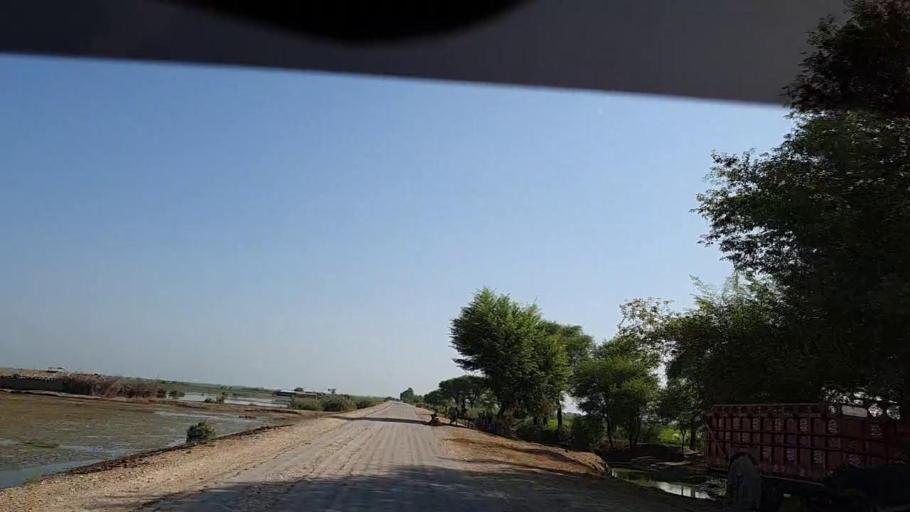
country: PK
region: Sindh
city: Tangwani
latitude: 28.3609
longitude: 69.0130
